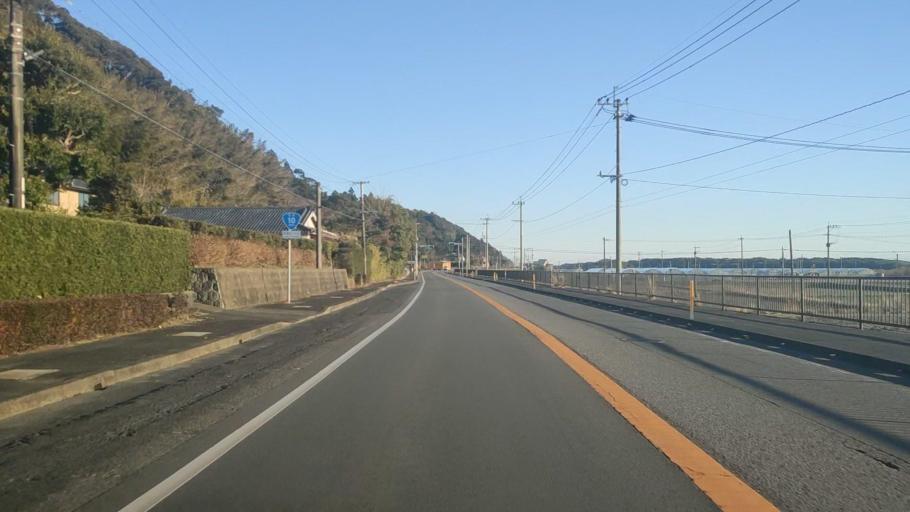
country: JP
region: Miyazaki
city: Takanabe
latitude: 32.0917
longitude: 131.5149
